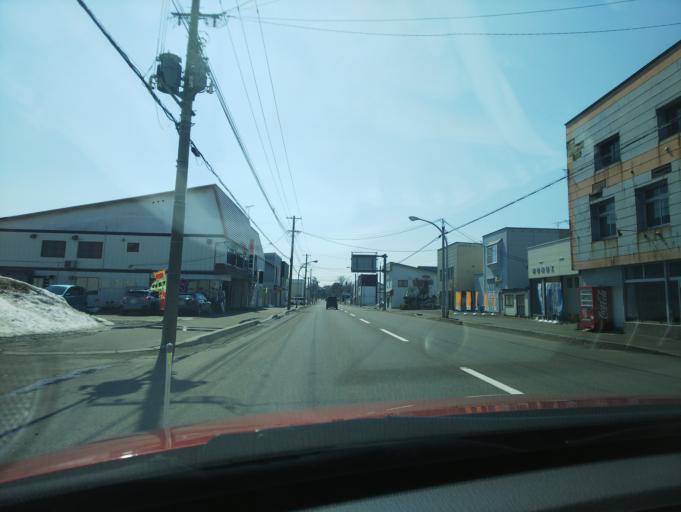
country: JP
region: Hokkaido
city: Nayoro
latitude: 44.2925
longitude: 142.4198
